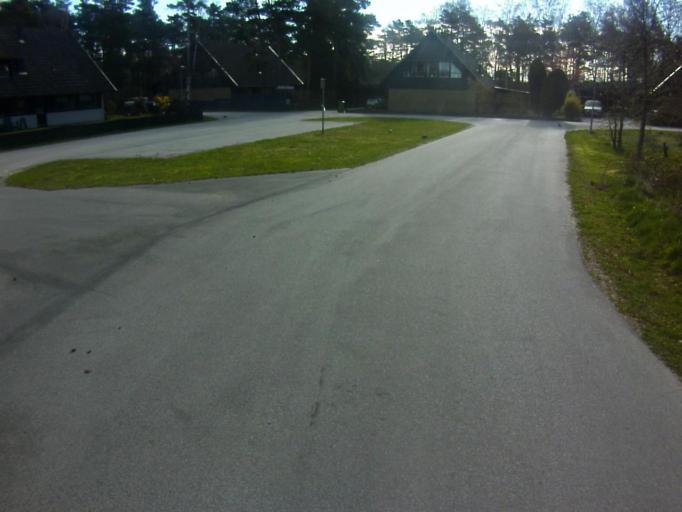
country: SE
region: Skane
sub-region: Kavlinge Kommun
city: Hofterup
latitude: 55.8033
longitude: 12.9758
